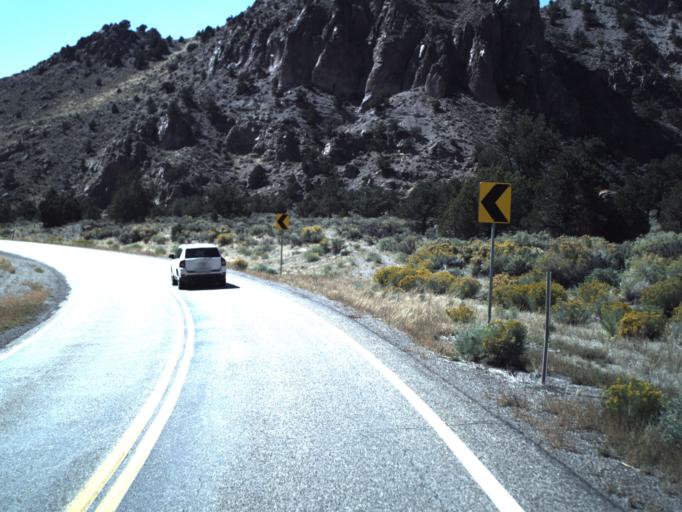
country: US
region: Utah
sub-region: Piute County
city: Junction
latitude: 38.1973
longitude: -112.1255
